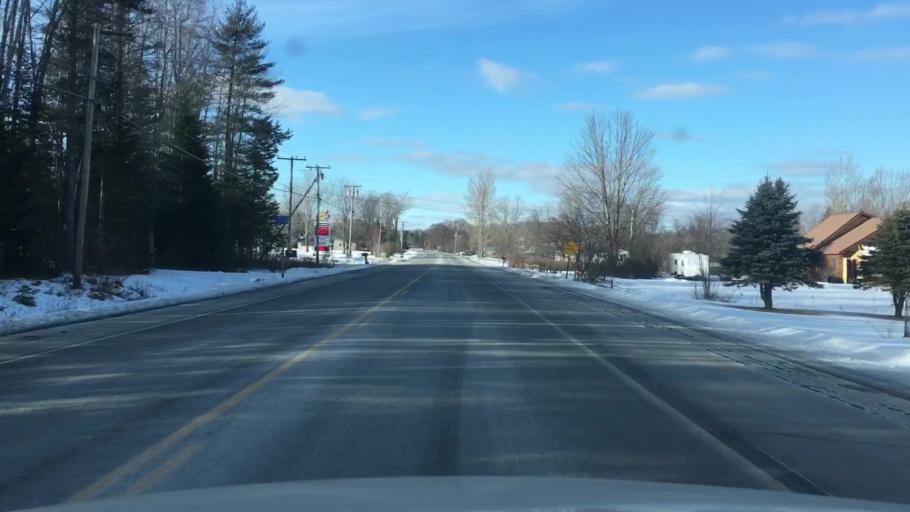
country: US
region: Maine
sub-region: Penobscot County
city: Eddington
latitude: 44.8228
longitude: -68.6509
